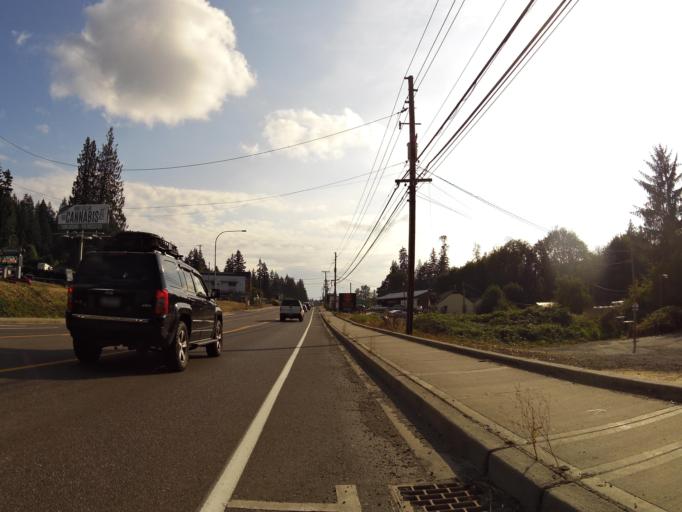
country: US
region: Washington
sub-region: Mason County
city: Belfair
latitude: 47.4484
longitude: -122.8292
